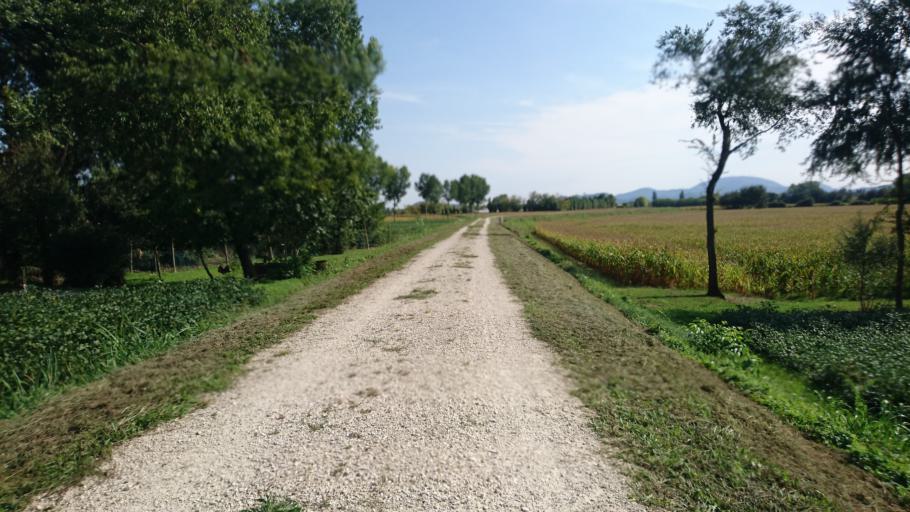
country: IT
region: Veneto
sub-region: Provincia di Padova
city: Veggiano
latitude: 45.4292
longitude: 11.7283
